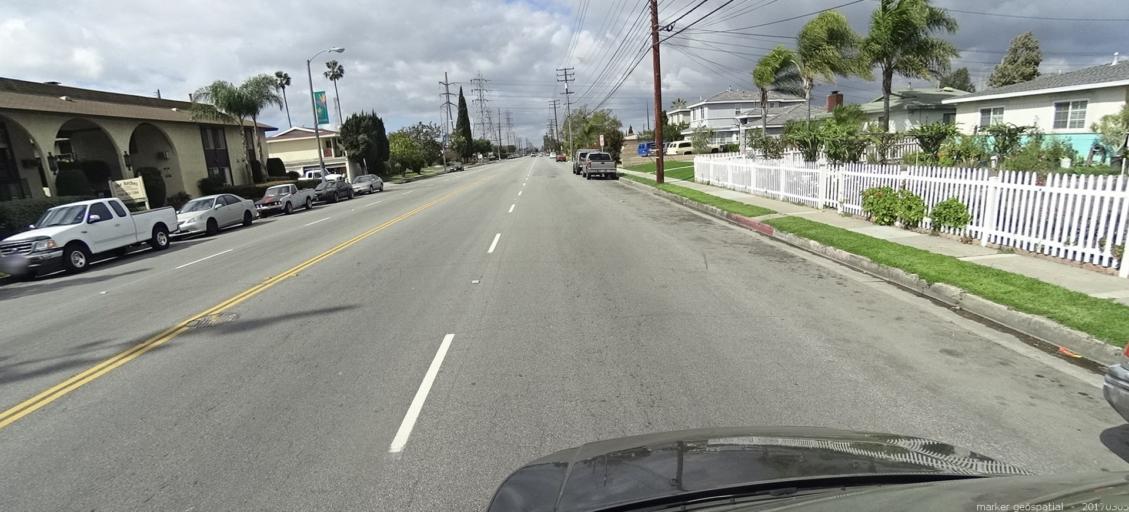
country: US
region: California
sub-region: Orange County
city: Stanton
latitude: 33.8104
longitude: -117.9774
